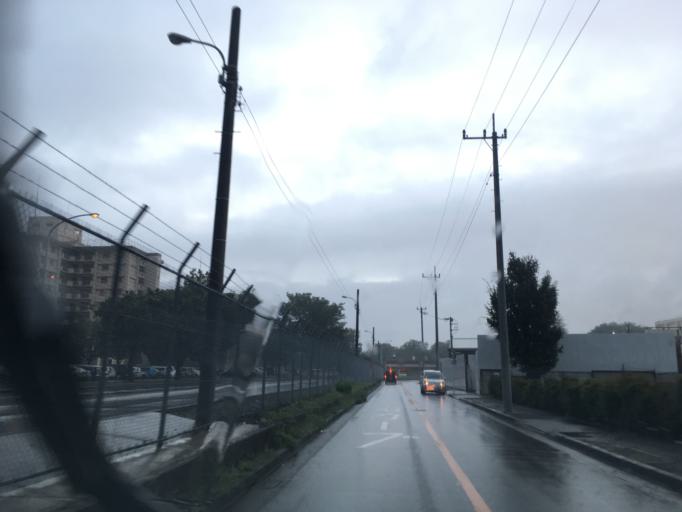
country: JP
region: Tokyo
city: Fussa
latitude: 35.7381
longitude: 139.3617
